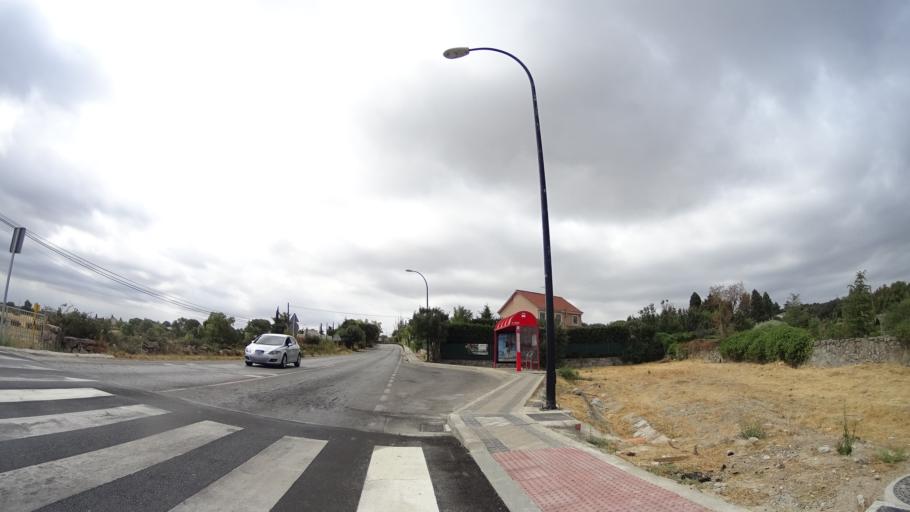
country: ES
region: Madrid
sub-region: Provincia de Madrid
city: Galapagar
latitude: 40.5888
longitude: -4.0118
